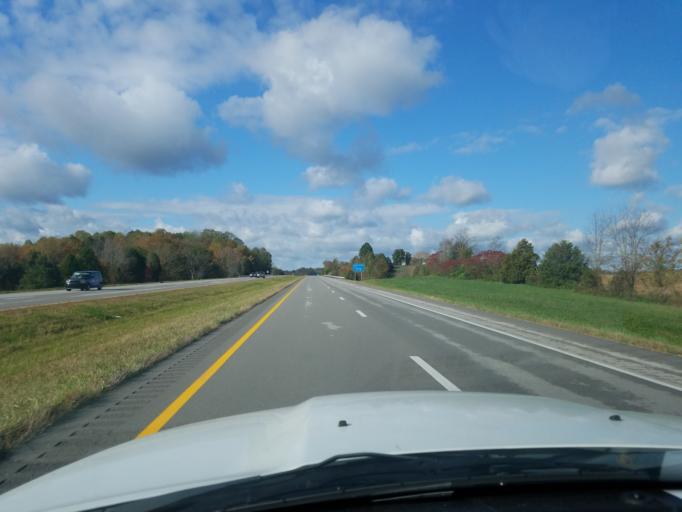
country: US
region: Kentucky
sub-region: Pulaski County
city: Somerset
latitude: 37.0954
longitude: -84.7864
